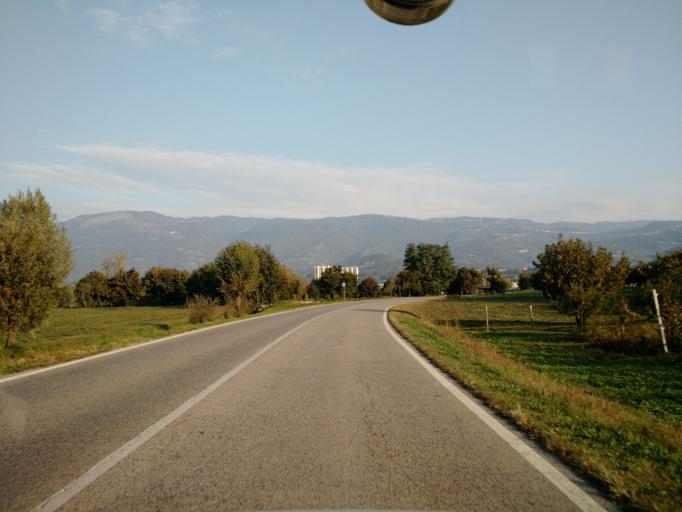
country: IT
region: Veneto
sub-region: Provincia di Vicenza
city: Zugliano
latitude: 45.7206
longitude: 11.5418
